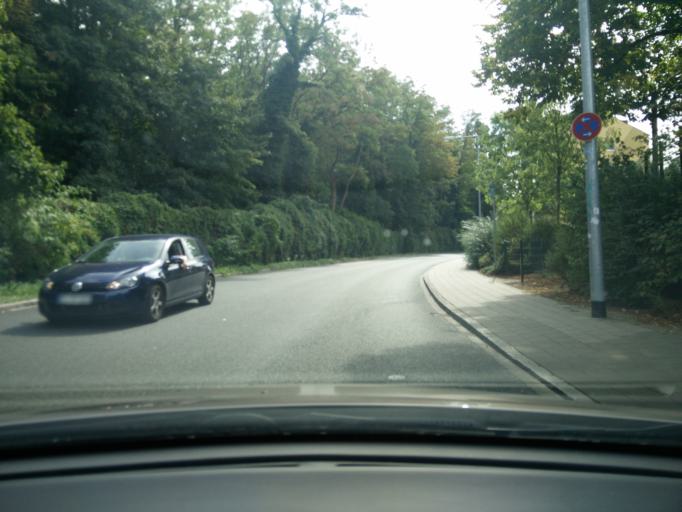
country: DE
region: Bavaria
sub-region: Regierungsbezirk Mittelfranken
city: Furth
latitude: 49.4782
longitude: 10.9821
